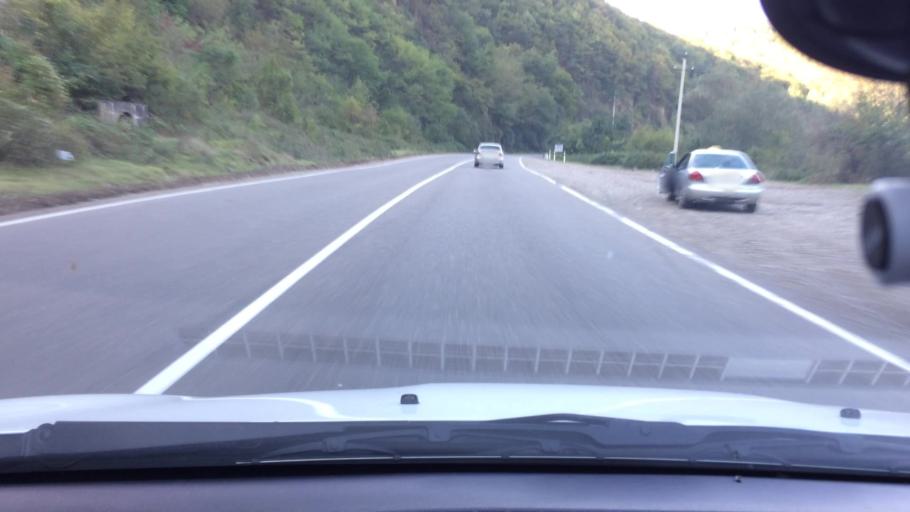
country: GE
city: Shorapani
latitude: 42.0948
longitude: 43.1181
